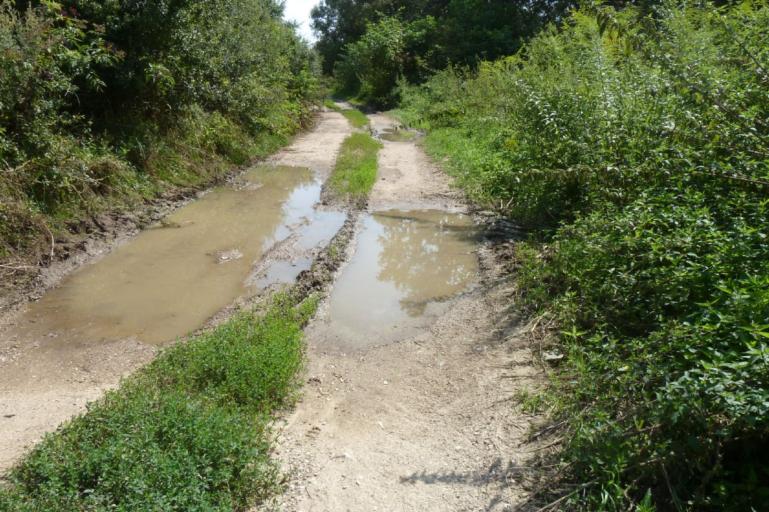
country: HU
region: Pest
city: Acsa
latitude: 47.8391
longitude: 19.3028
